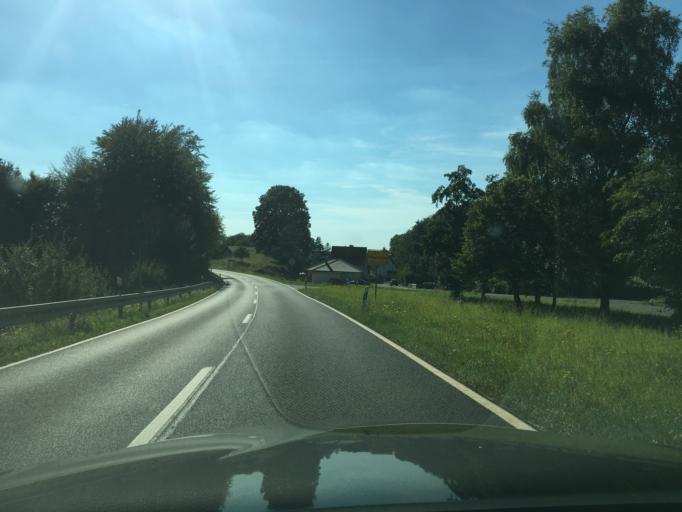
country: DE
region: Bavaria
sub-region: Upper Franconia
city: Hiltpoltstein
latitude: 49.6614
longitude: 11.3295
